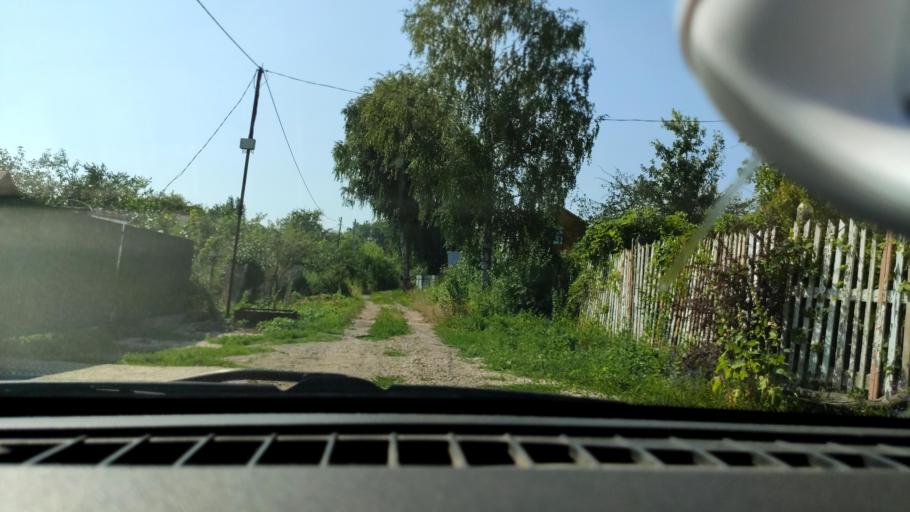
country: RU
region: Samara
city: Petra-Dubrava
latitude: 53.2686
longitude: 50.2983
